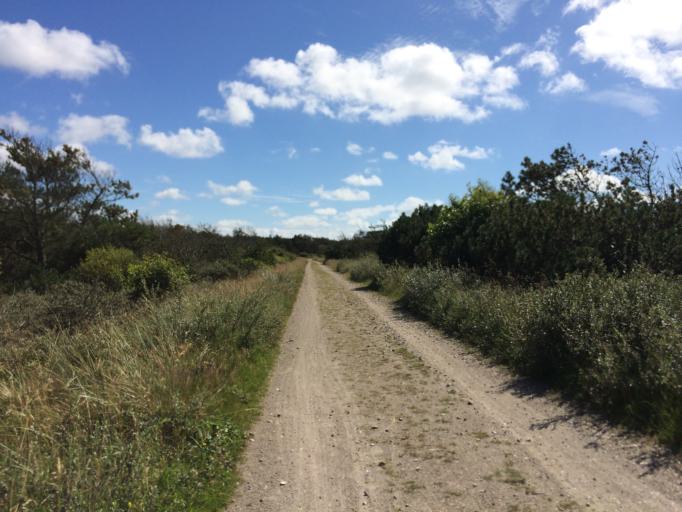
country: DK
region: Central Jutland
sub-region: Holstebro Kommune
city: Ulfborg
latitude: 56.3130
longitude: 8.1325
